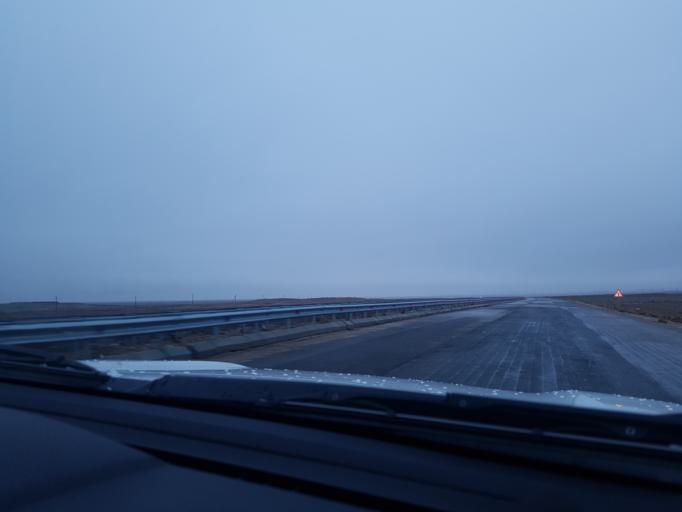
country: TM
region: Balkan
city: Balkanabat
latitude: 39.8947
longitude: 54.0168
